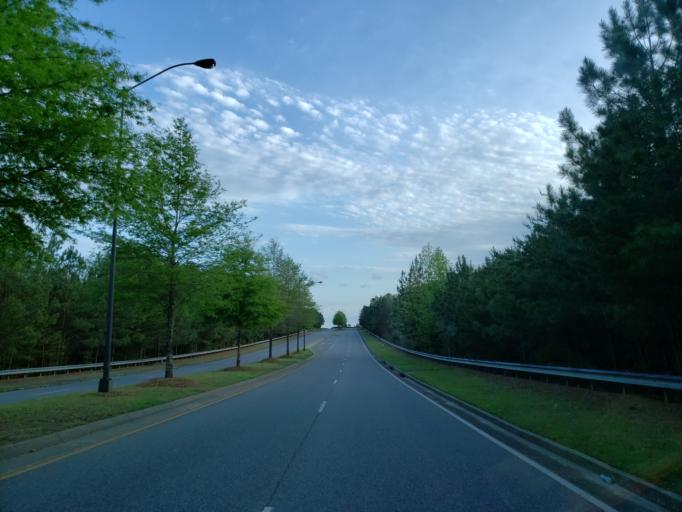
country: US
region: Georgia
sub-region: Cherokee County
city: Canton
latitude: 34.2779
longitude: -84.4693
